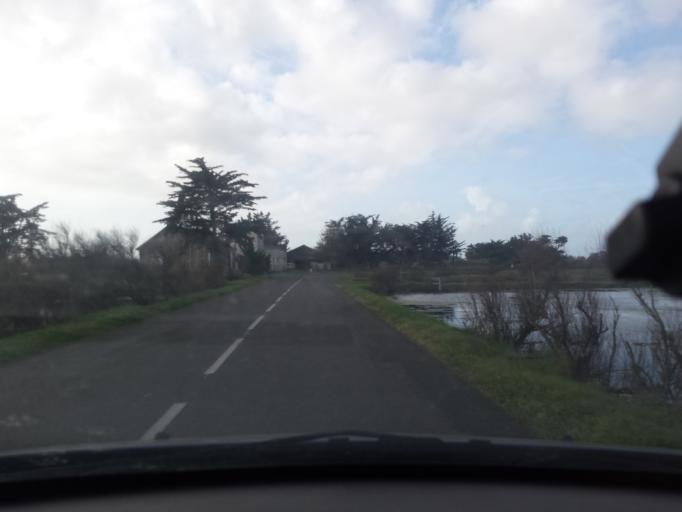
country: FR
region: Pays de la Loire
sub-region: Departement de la Vendee
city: Olonne-sur-Mer
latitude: 46.5563
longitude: -1.7890
